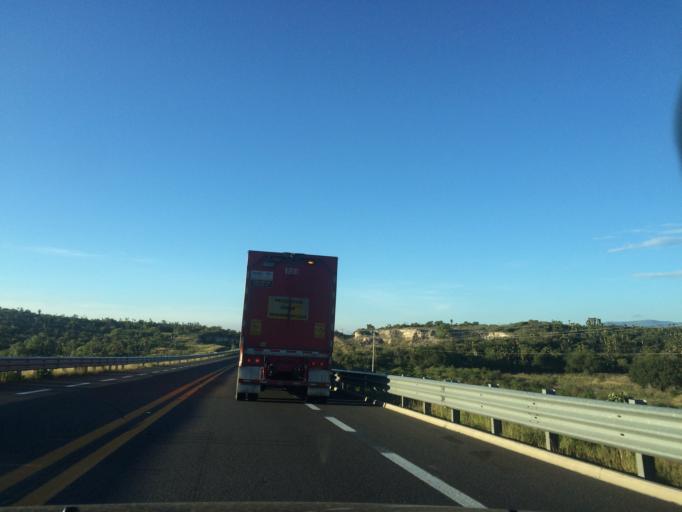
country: MX
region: Puebla
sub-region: Tehuacan
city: Magdalena Cuayucatepec
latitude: 18.5799
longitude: -97.4655
